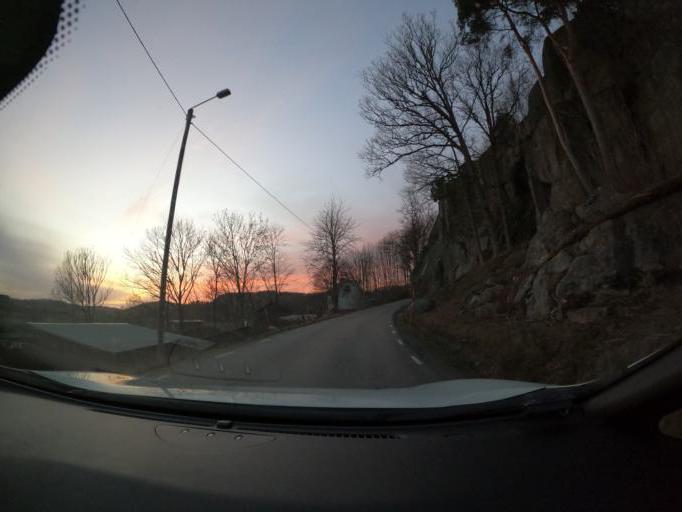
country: SE
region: Vaestra Goetaland
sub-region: Harryda Kommun
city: Molnlycke
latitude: 57.6060
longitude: 12.1565
